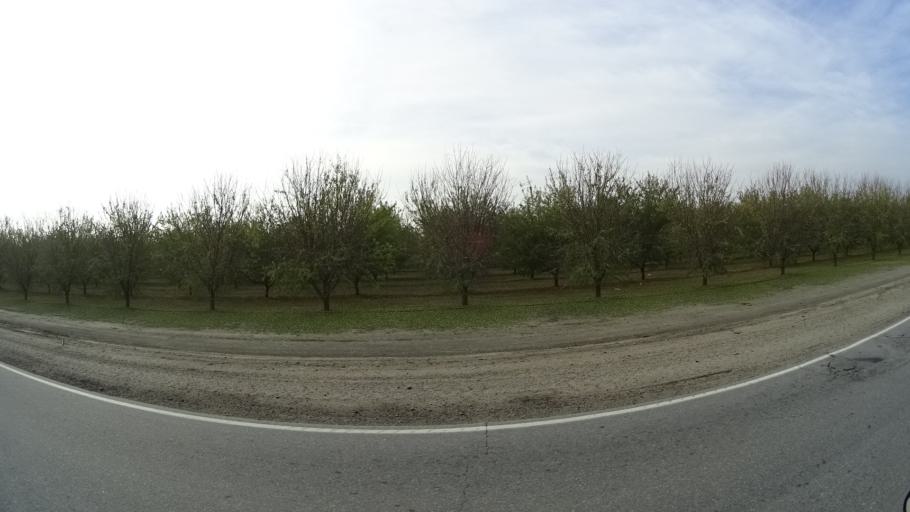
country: US
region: California
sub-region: Kern County
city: Greenacres
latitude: 35.2721
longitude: -119.1283
